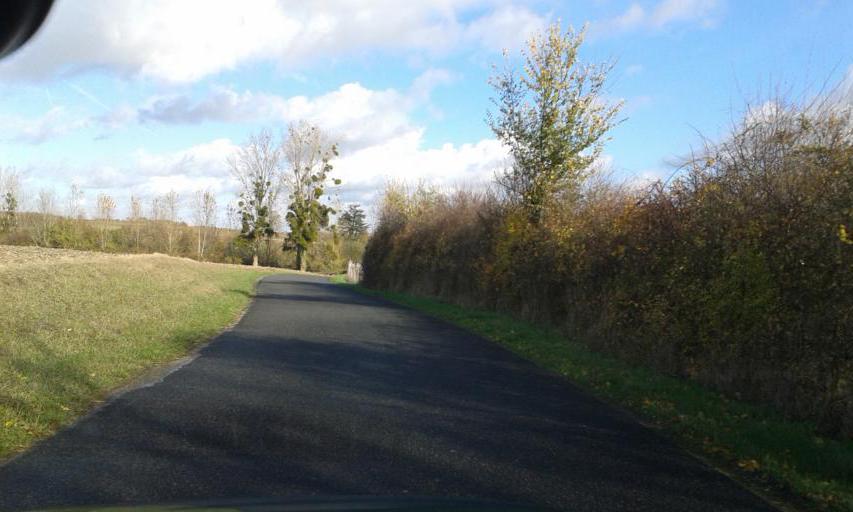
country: FR
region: Centre
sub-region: Departement du Loir-et-Cher
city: Saint-Laurent-Nouan
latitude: 47.7401
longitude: 1.5977
